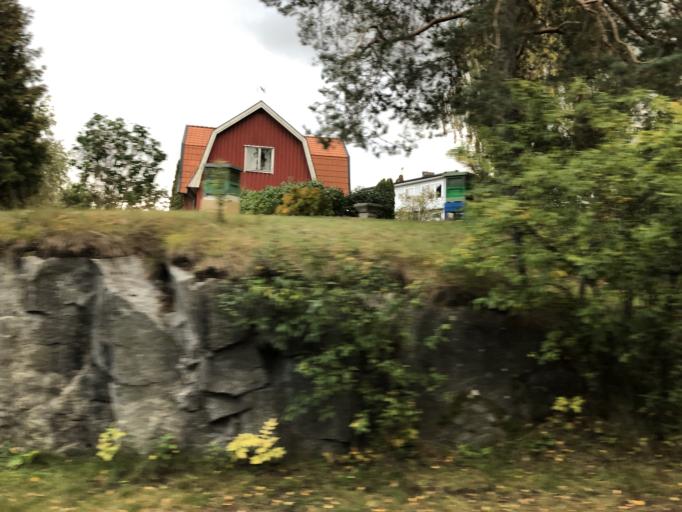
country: SE
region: Stockholm
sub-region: Jarfalla Kommun
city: Jakobsberg
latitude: 59.4296
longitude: 17.8150
